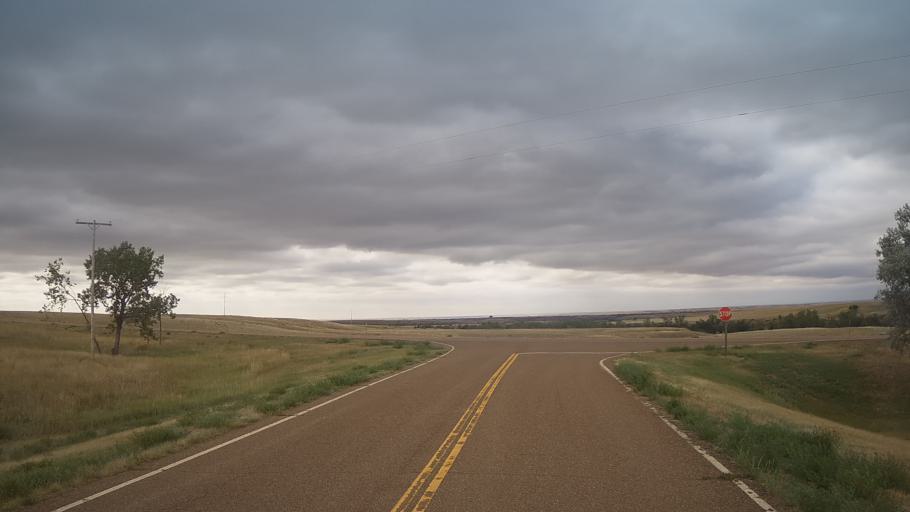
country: US
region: Montana
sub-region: Valley County
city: Glasgow
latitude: 48.3696
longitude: -106.7923
